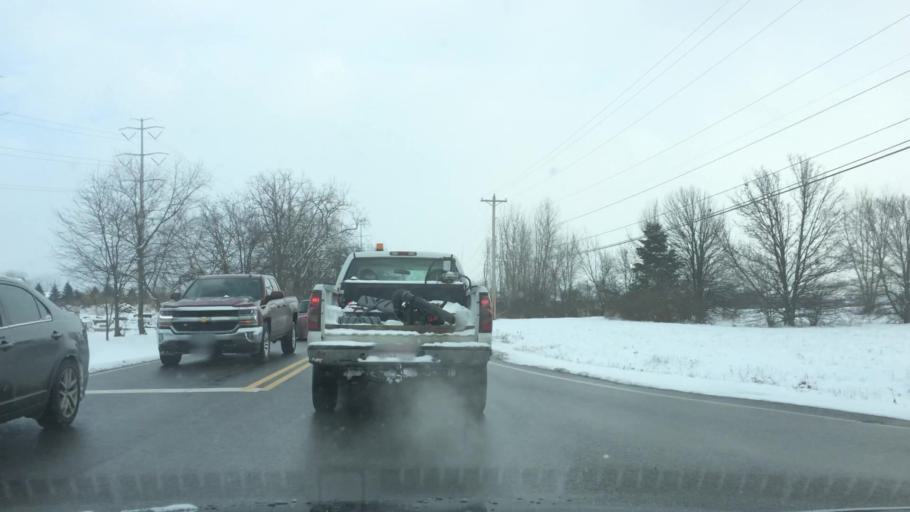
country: US
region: Ohio
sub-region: Franklin County
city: Hilliard
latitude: 40.0194
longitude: -83.1404
